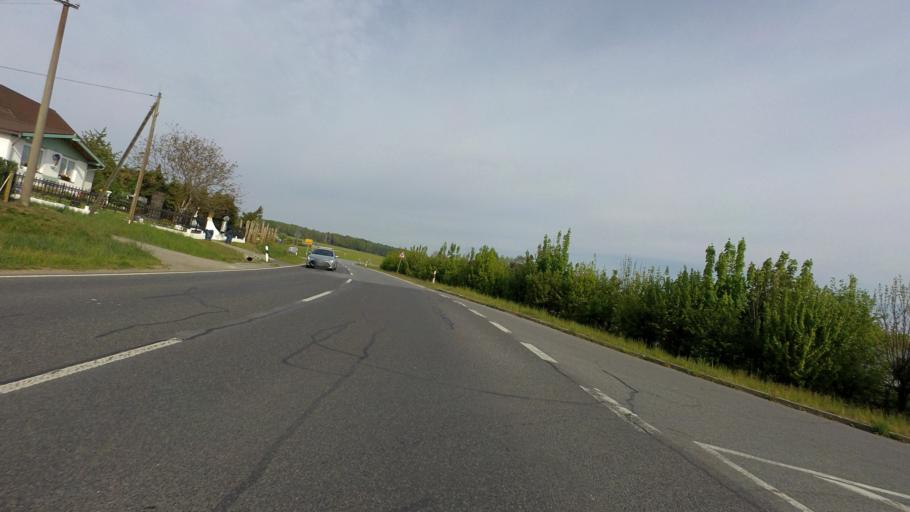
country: DE
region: Saxony
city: Stolpen
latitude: 51.0592
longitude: 14.0614
